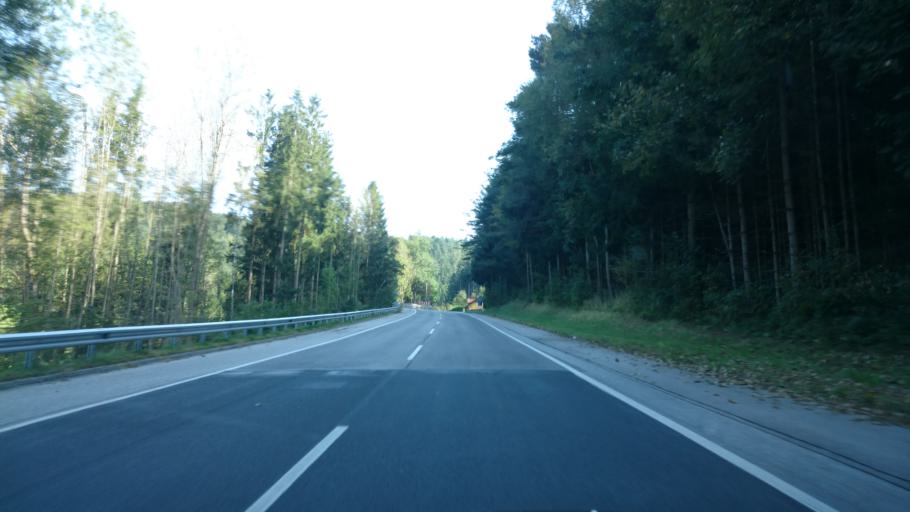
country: AT
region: Lower Austria
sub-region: Politischer Bezirk Neunkirchen
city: Monichkirchen
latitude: 47.5419
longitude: 16.0748
